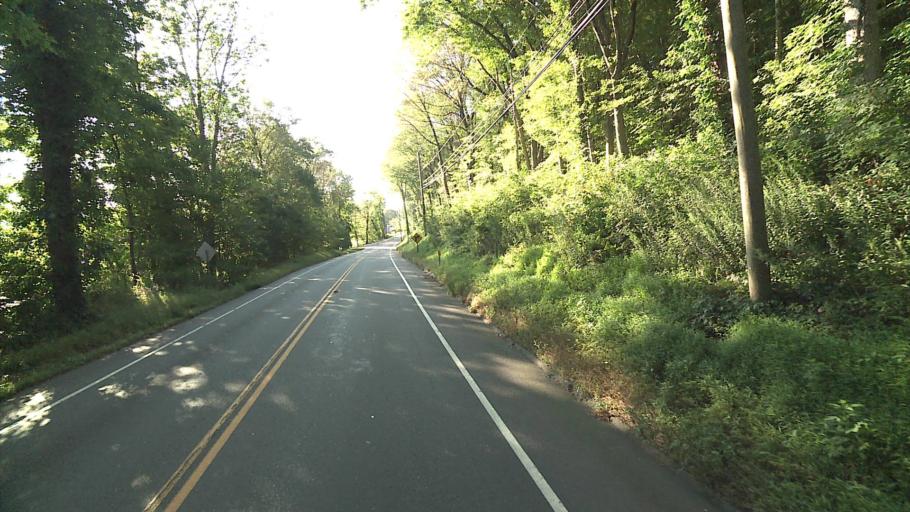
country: US
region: Connecticut
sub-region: New London County
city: Baltic
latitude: 41.6076
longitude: -72.1394
